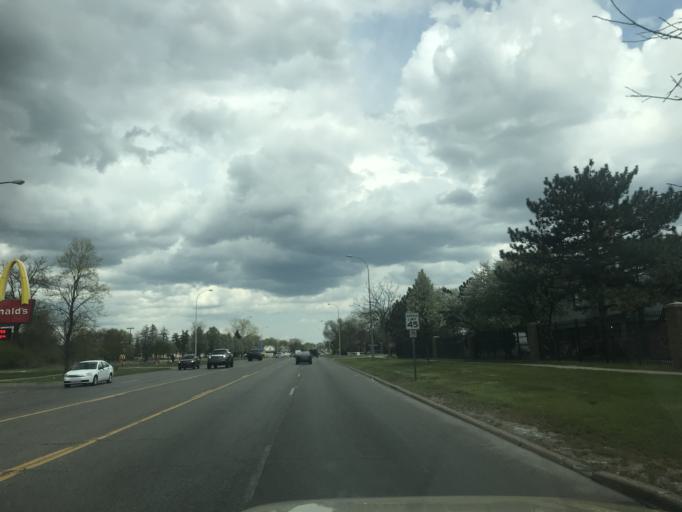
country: US
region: Michigan
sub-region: Wayne County
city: Taylor
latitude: 42.1964
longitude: -83.3006
